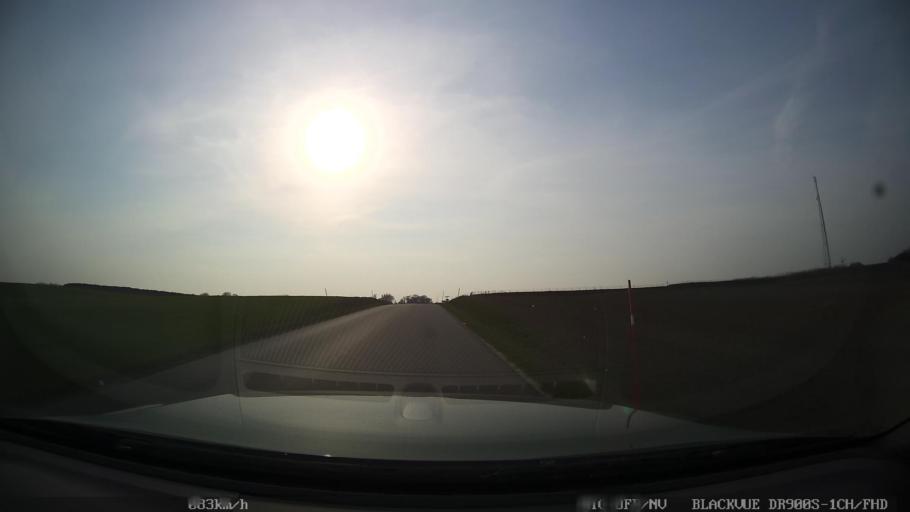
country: SE
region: Skane
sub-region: Ystads Kommun
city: Ystad
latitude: 55.4593
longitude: 13.7902
